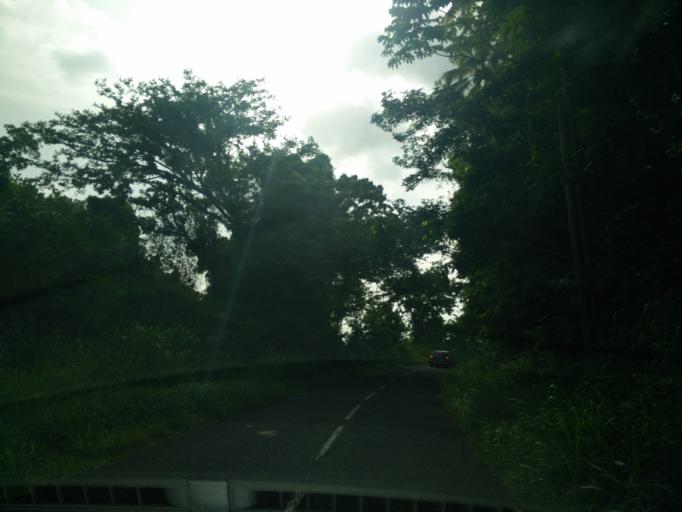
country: MQ
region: Martinique
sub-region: Martinique
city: Saint-Pierre
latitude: 14.8244
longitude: -61.2269
